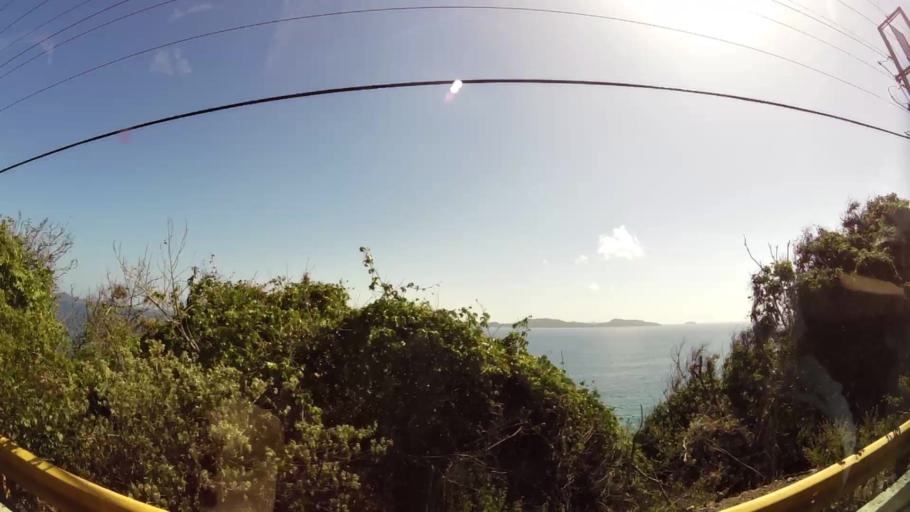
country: VG
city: Tortola
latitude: 18.4125
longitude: -64.5904
